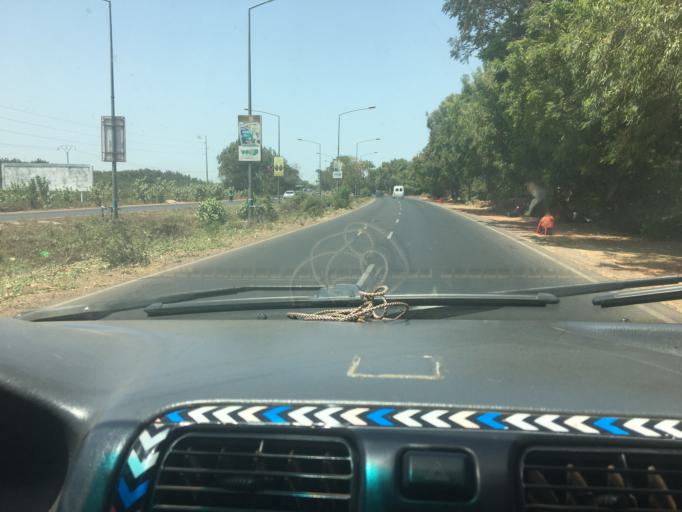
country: GM
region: Banjul
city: Bakau
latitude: 13.4694
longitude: -16.6388
